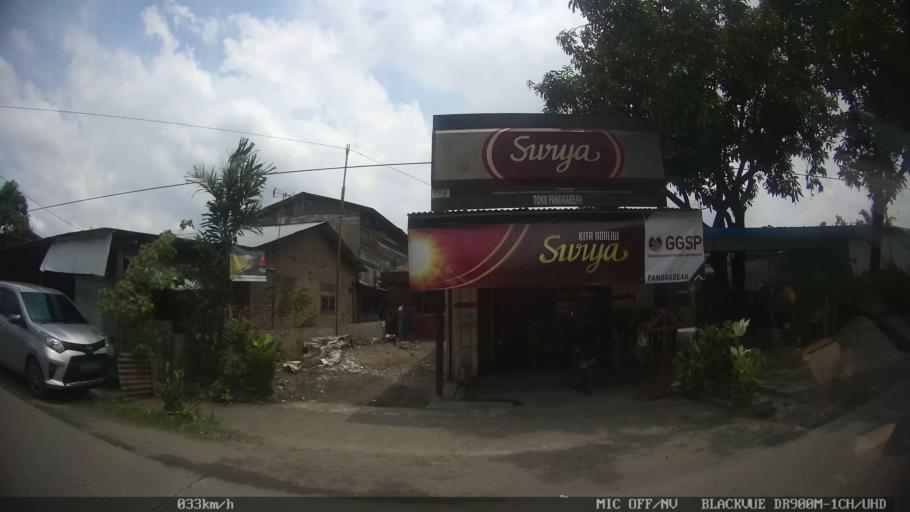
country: ID
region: North Sumatra
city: Medan
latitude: 3.6426
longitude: 98.6793
